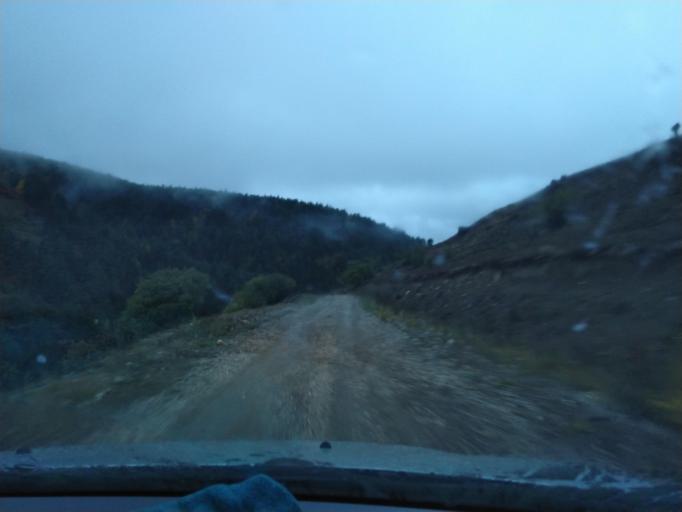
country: RU
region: North Ossetia
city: Tarskoye
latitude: 42.8250
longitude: 44.9755
